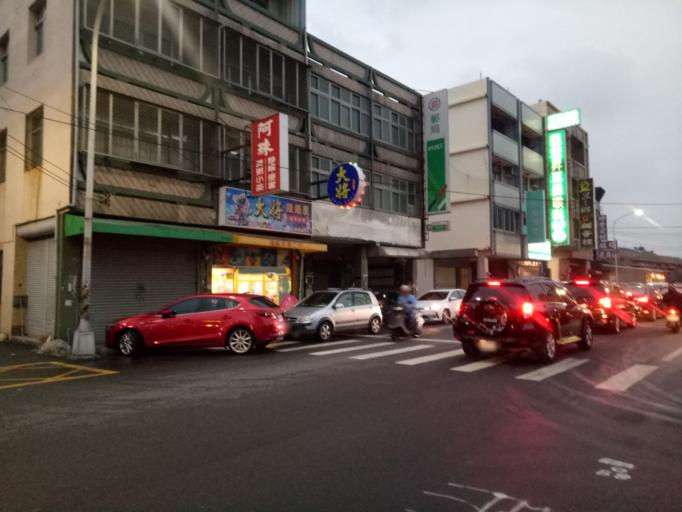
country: TW
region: Taiwan
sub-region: Changhua
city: Chang-hua
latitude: 24.2481
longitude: 120.5384
